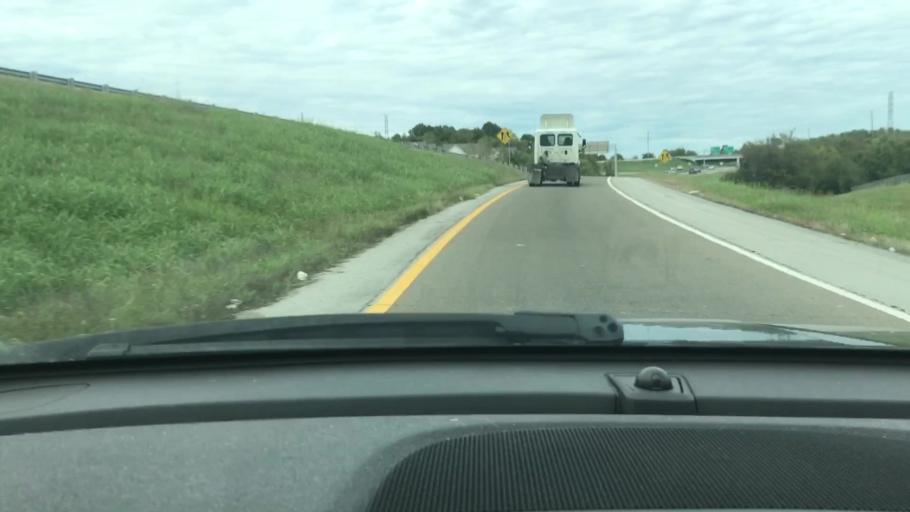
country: US
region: Tennessee
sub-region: Sumner County
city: Hendersonville
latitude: 36.3084
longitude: -86.6568
